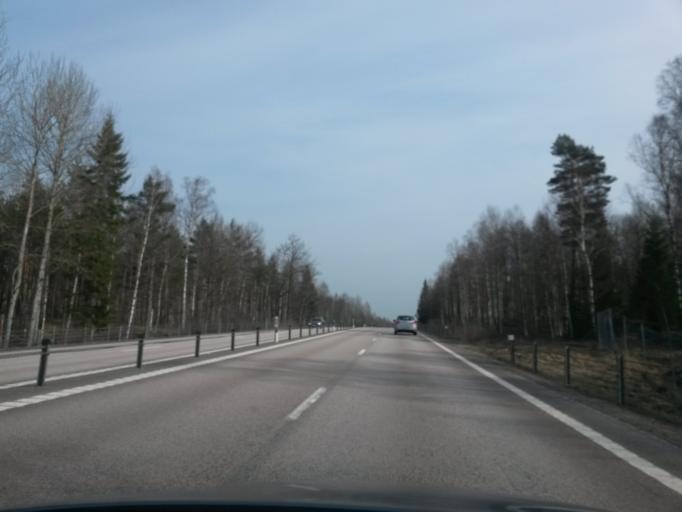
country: SE
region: Vaestra Goetaland
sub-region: Toreboda Kommun
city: Toereboda
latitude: 58.7698
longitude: 13.9898
